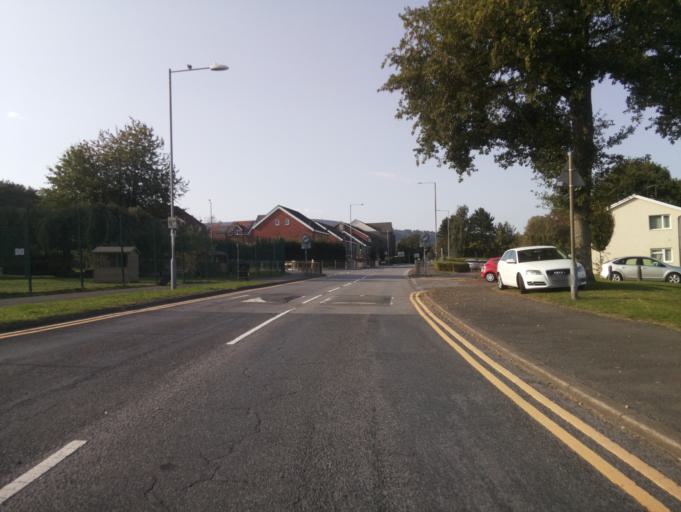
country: GB
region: Wales
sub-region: Torfaen County Borough
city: Cwmbran
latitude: 51.6492
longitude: -3.0224
